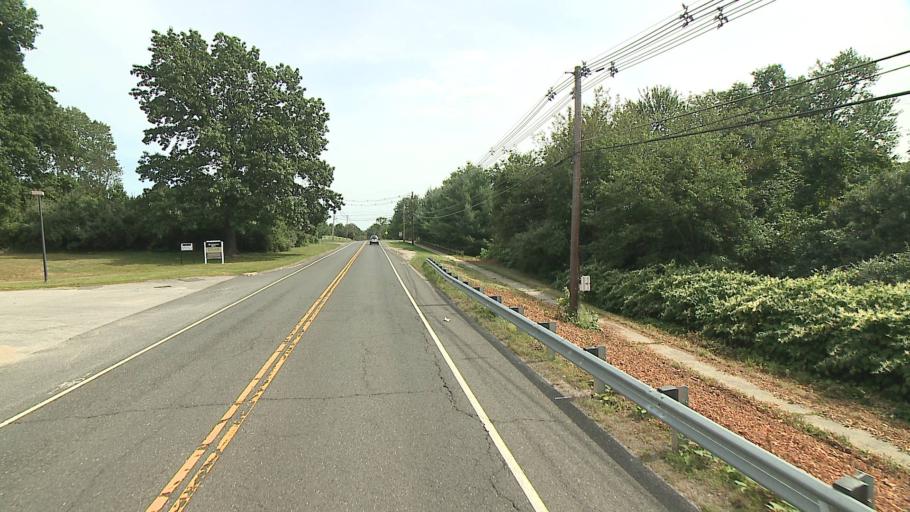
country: US
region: Connecticut
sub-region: Litchfield County
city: Watertown
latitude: 41.6136
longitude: -73.0967
